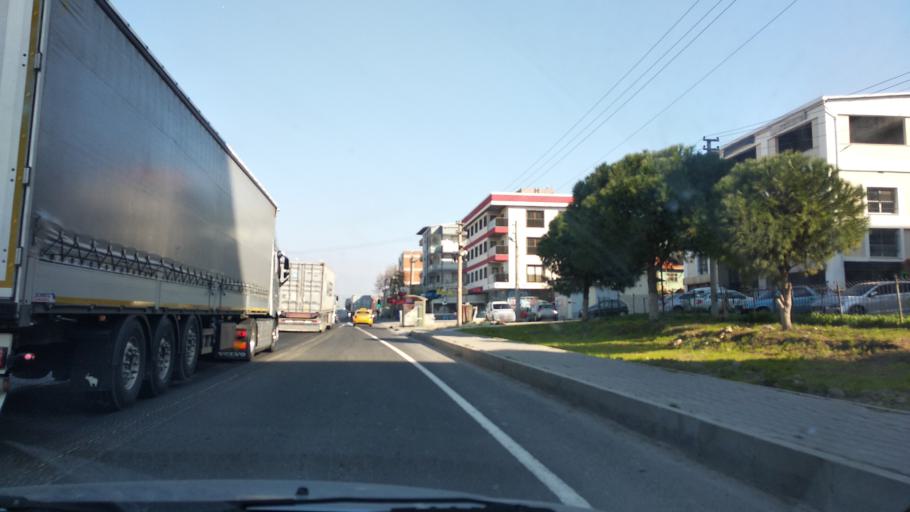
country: TR
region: Izmir
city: Menemen
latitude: 38.5731
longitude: 27.0598
